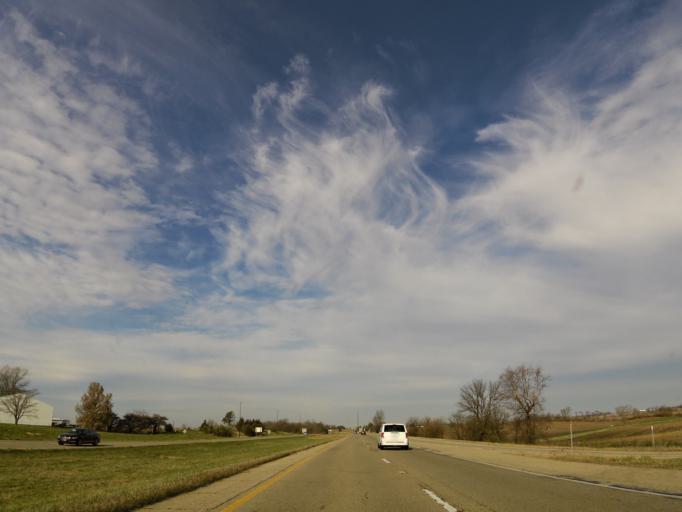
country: US
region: Illinois
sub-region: McLean County
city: Danvers
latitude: 40.5829
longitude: -89.1425
